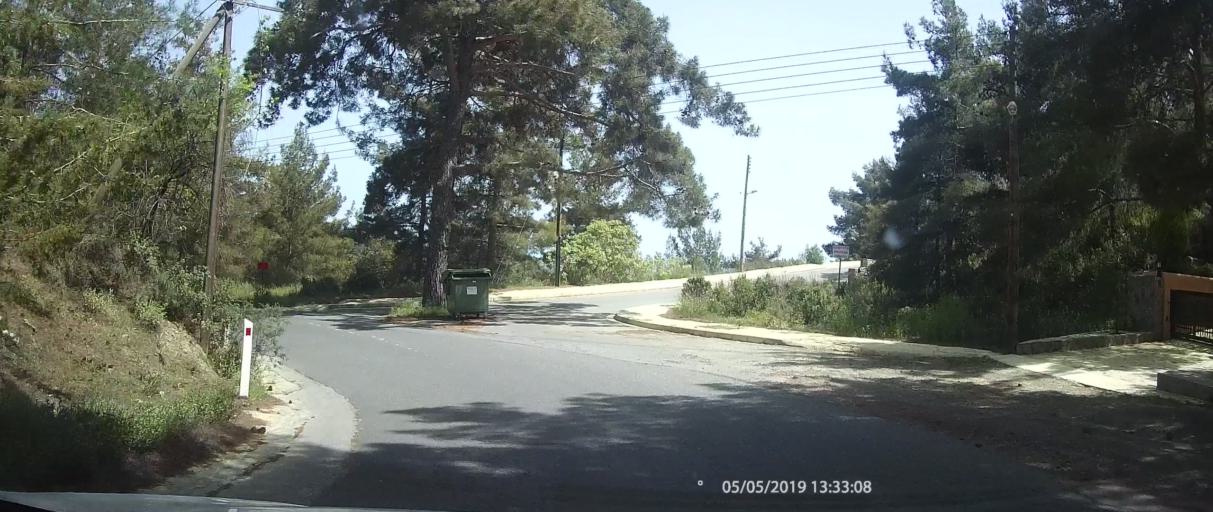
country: CY
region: Lefkosia
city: Kakopetria
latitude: 34.8867
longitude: 32.8544
